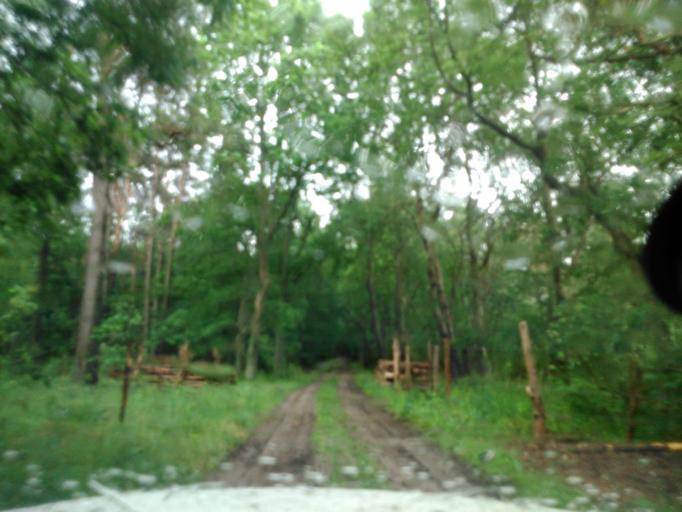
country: PL
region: Pomeranian Voivodeship
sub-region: Powiat slupski
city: Smoldzino
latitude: 54.6386
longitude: 17.2722
